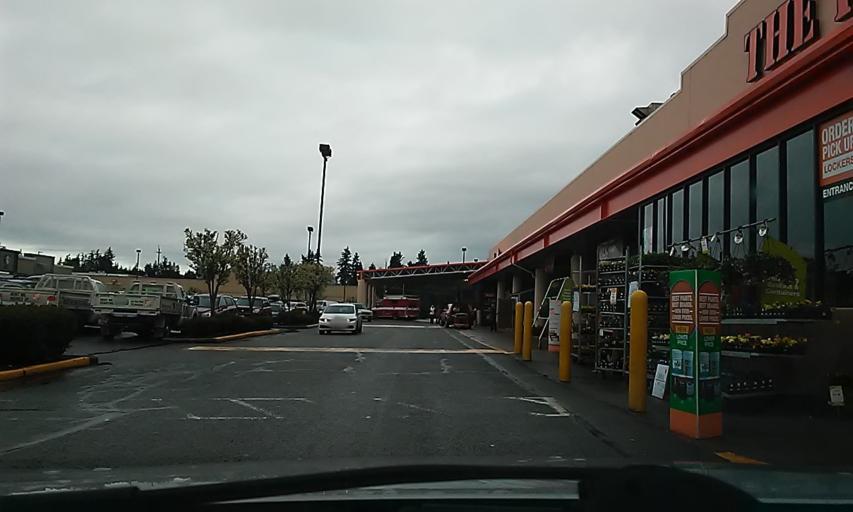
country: US
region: Washington
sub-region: Snohomish County
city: Esperance
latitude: 47.7757
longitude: -122.3427
